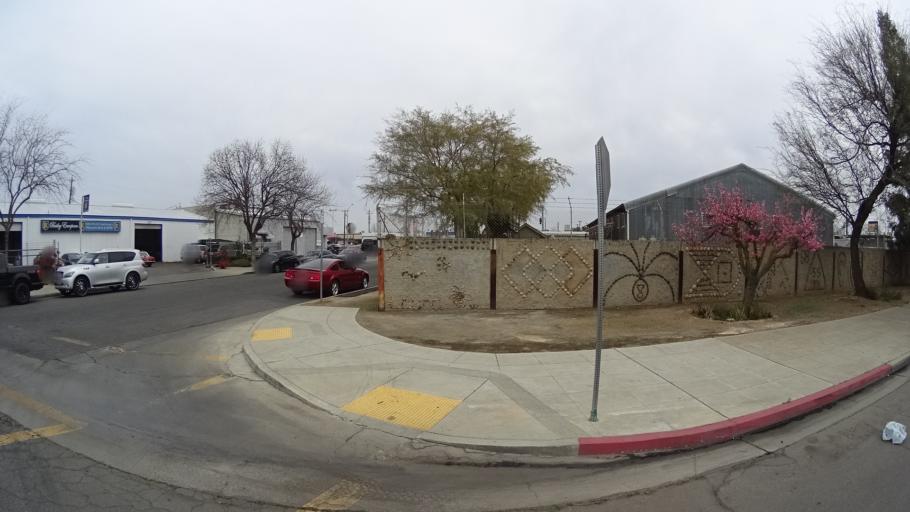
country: US
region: California
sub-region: Fresno County
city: Clovis
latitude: 36.8408
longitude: -119.7916
